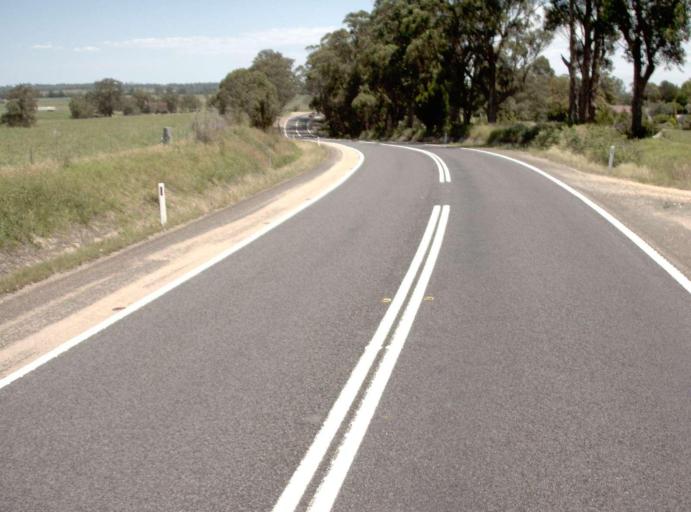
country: AU
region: Victoria
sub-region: East Gippsland
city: Lakes Entrance
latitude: -37.7033
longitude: 148.5161
